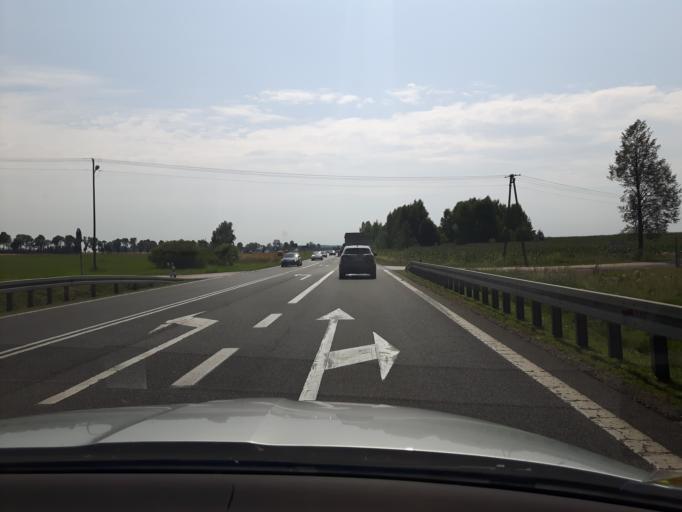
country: PL
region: Masovian Voivodeship
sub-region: Powiat mlawski
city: Wieczfnia Koscielna
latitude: 53.1874
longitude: 20.4312
